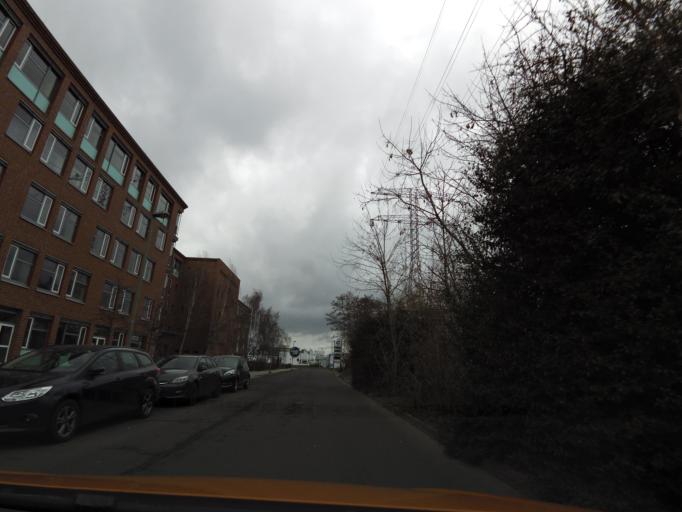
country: DE
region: Berlin
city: Biesdorf
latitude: 52.5297
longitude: 13.5337
